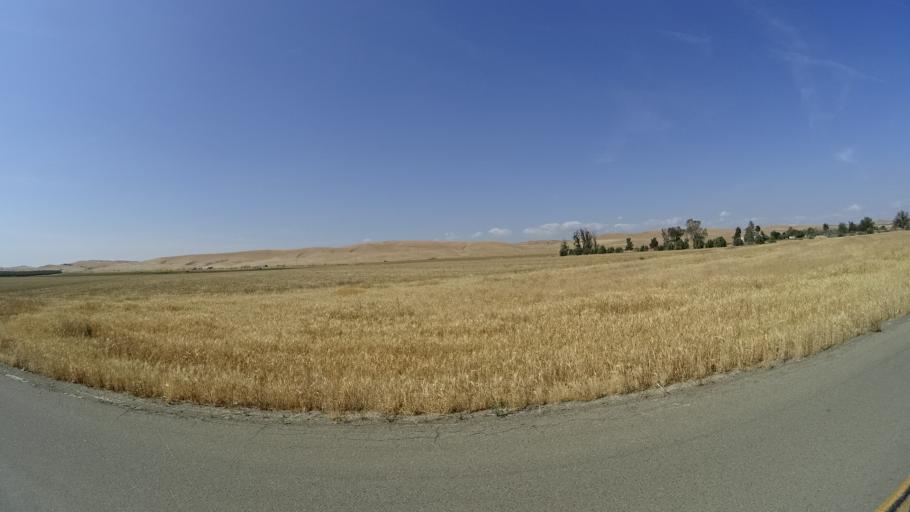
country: US
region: California
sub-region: Kings County
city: Avenal
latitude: 36.0729
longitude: -120.0794
